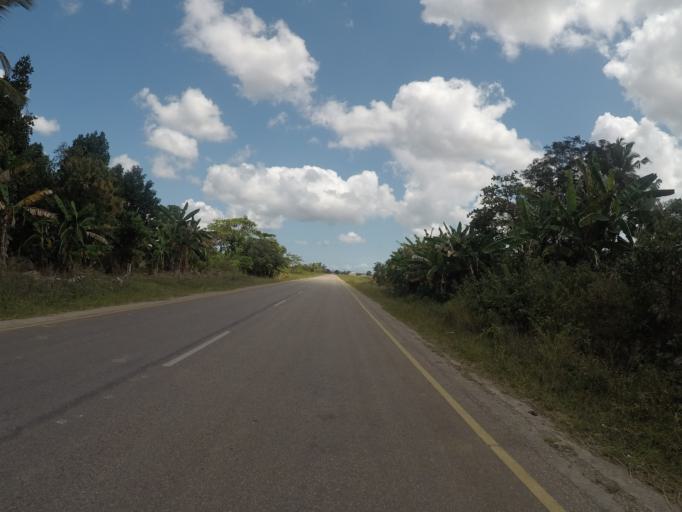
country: TZ
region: Zanzibar Central/South
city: Koani
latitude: -6.1840
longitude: 39.3718
